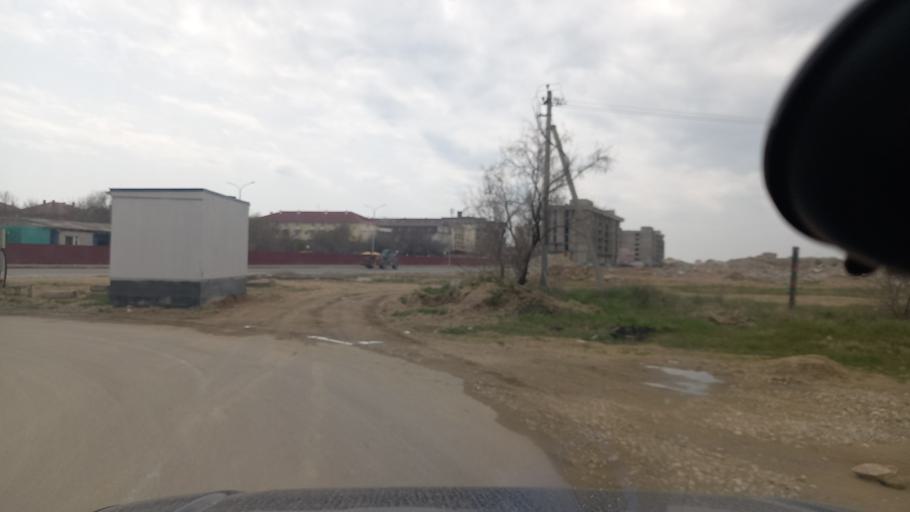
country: RU
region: Krasnodarskiy
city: Vityazevo
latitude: 44.9934
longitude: 37.2435
